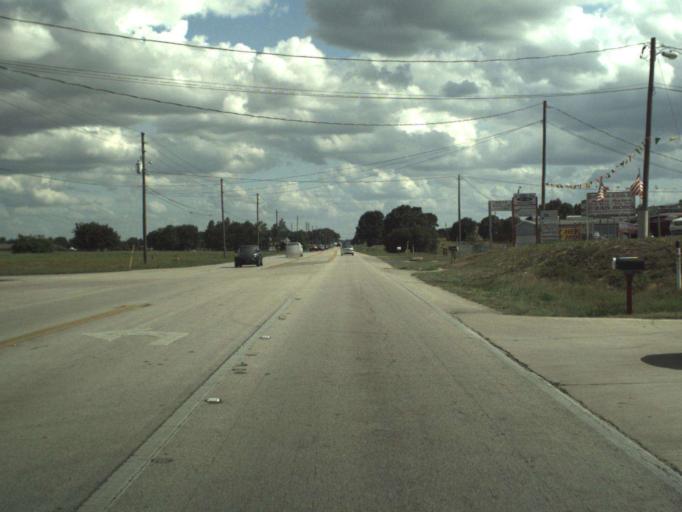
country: US
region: Florida
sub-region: Marion County
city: Silver Springs Shores
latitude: 29.1022
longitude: -82.0536
